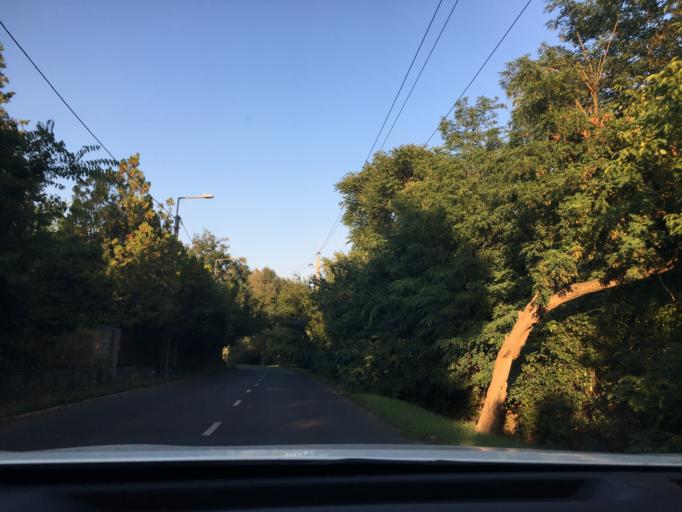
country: HU
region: Budapest
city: Budapest XVII. keruelet
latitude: 47.4860
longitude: 19.2631
